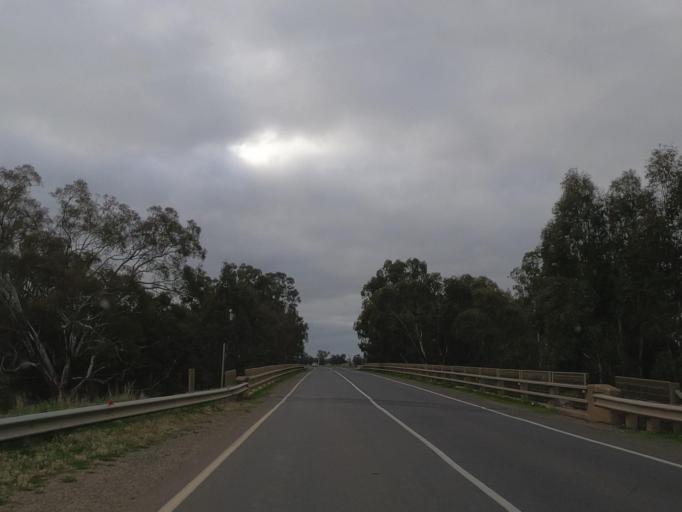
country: AU
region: Victoria
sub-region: Greater Bendigo
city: Long Gully
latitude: -36.4462
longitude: 143.9665
